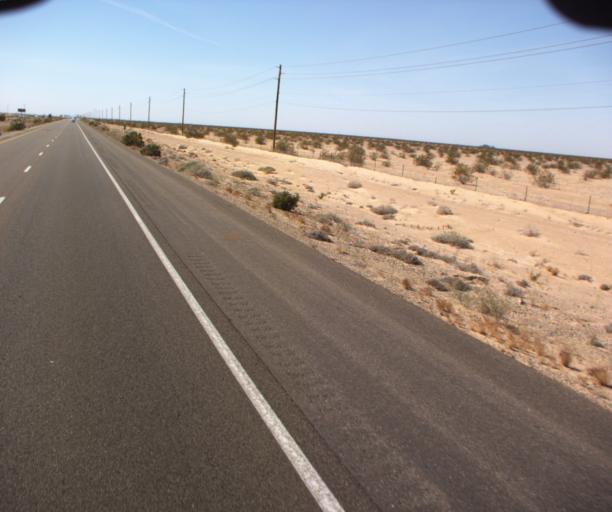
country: MX
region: Sonora
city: San Luis Rio Colorado
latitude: 32.4948
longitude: -114.6835
